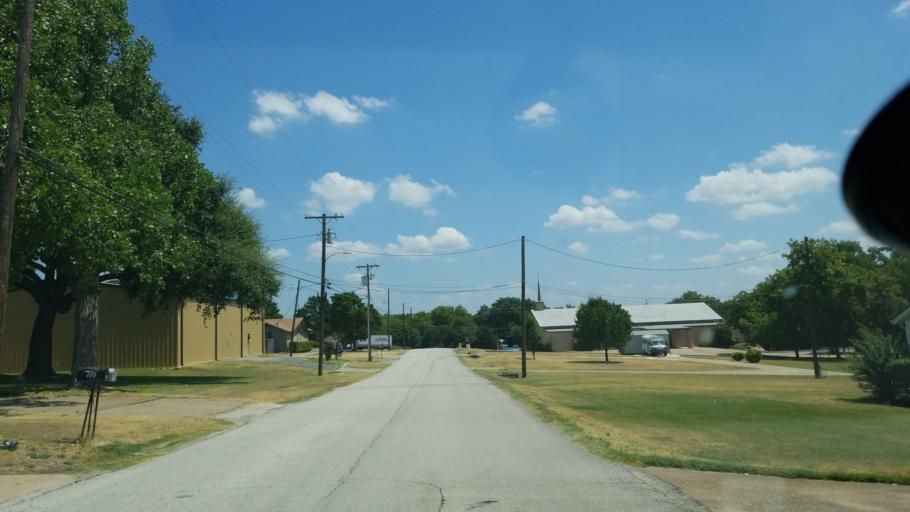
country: US
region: Texas
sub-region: Dallas County
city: Duncanville
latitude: 32.6719
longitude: -96.8933
